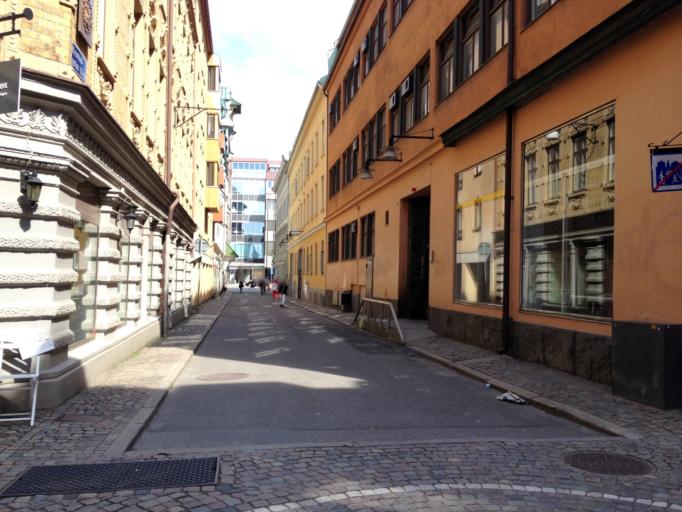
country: SE
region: Vaestra Goetaland
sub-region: Goteborg
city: Goeteborg
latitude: 57.7083
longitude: 11.9654
